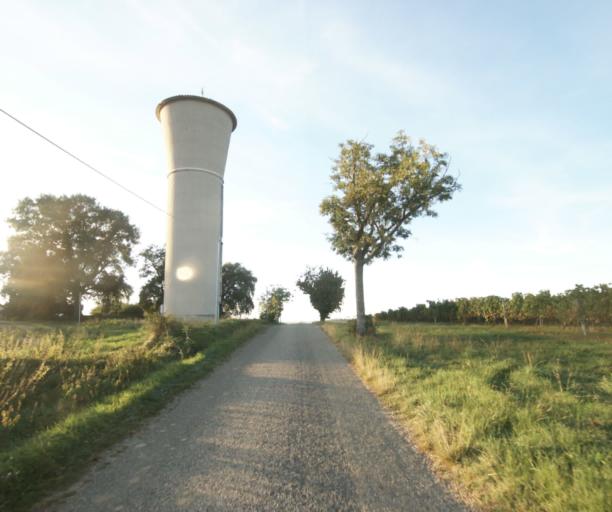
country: FR
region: Midi-Pyrenees
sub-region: Departement du Gers
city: Gondrin
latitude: 43.8453
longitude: 0.2540
